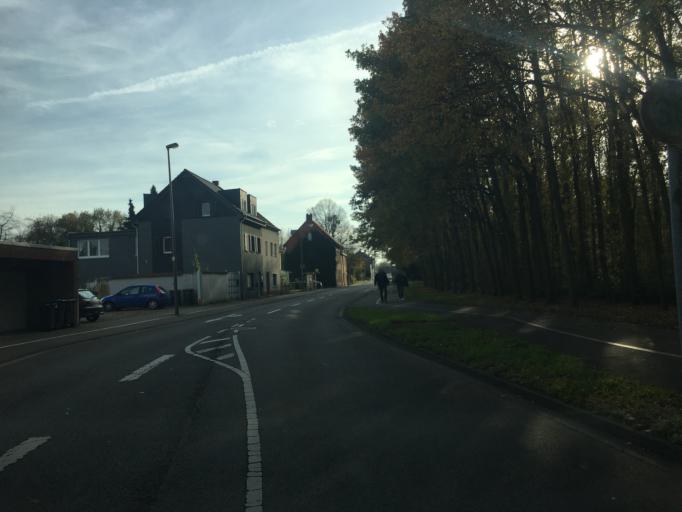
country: DE
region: North Rhine-Westphalia
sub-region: Regierungsbezirk Koln
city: Merheim
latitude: 50.9557
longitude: 7.0501
